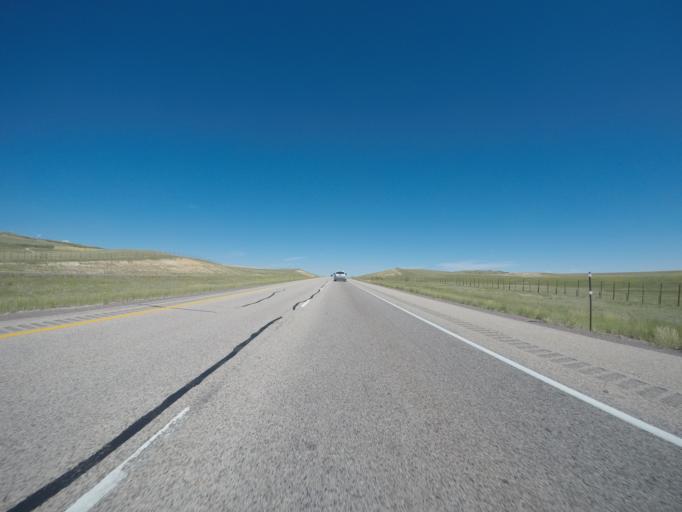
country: US
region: Wyoming
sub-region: Albany County
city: Laramie
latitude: 41.4927
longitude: -106.0397
